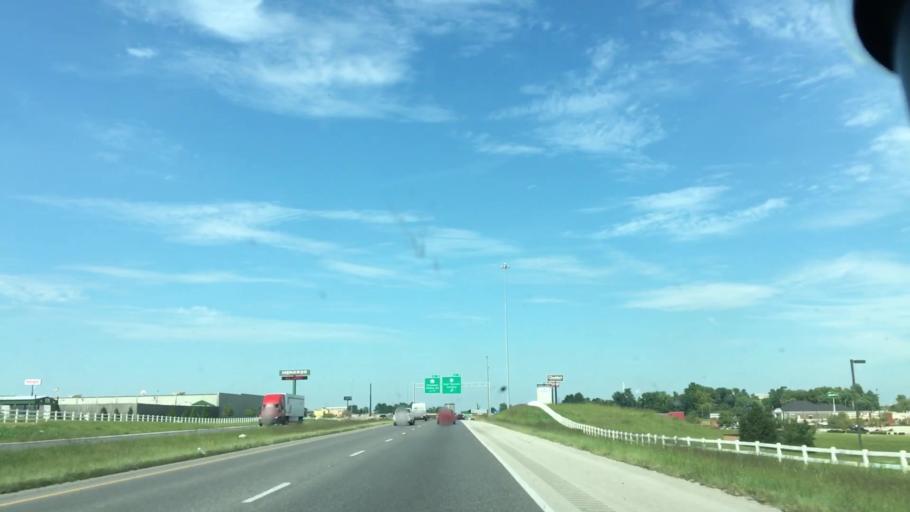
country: US
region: Kentucky
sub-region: Daviess County
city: Owensboro
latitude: 37.7515
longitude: -87.0712
